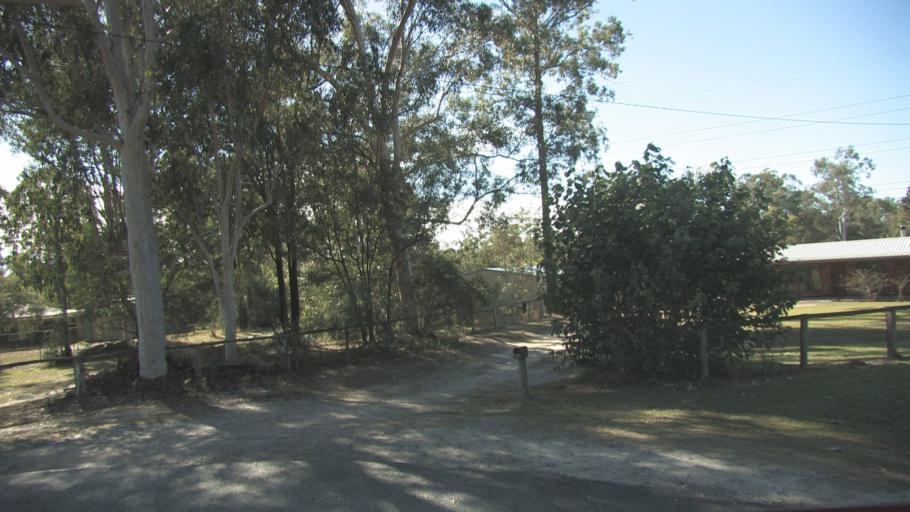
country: AU
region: Queensland
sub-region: Logan
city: Chambers Flat
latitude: -27.7799
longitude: 153.0786
